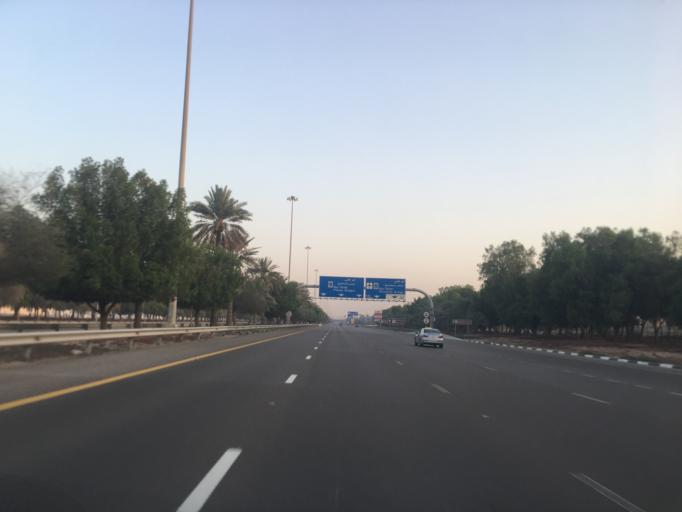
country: AE
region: Abu Dhabi
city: Abu Dhabi
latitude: 24.3801
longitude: 54.5480
